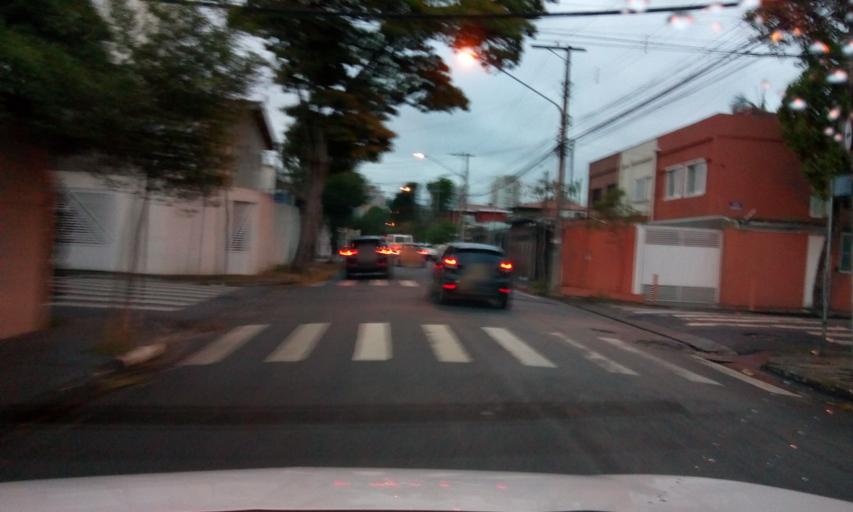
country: BR
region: Sao Paulo
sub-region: Sao Paulo
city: Sao Paulo
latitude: -23.6086
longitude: -46.6840
